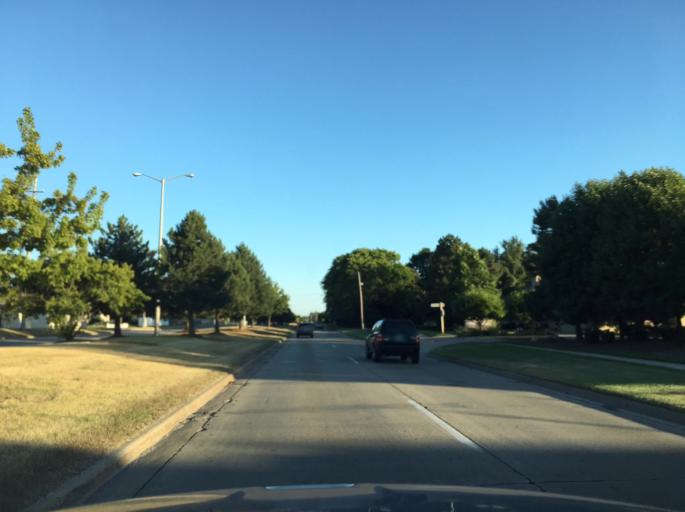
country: US
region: Michigan
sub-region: Macomb County
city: Utica
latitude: 42.6078
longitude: -82.9923
